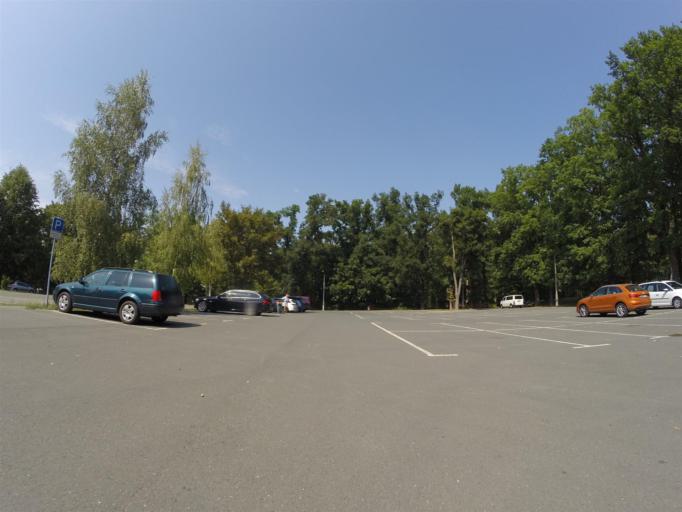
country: DE
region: Thuringia
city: Stadtroda
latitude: 50.8604
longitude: 11.7382
